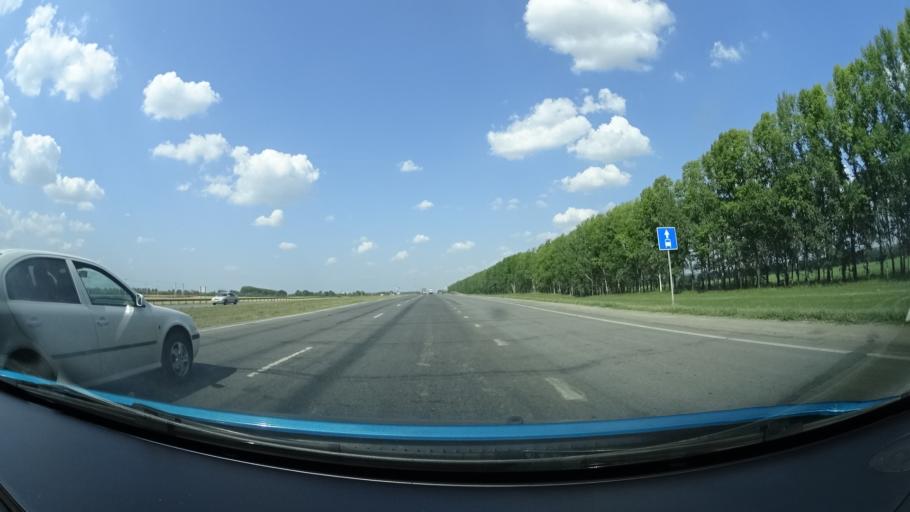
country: RU
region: Bashkortostan
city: Chishmy
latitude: 54.6555
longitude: 55.4853
